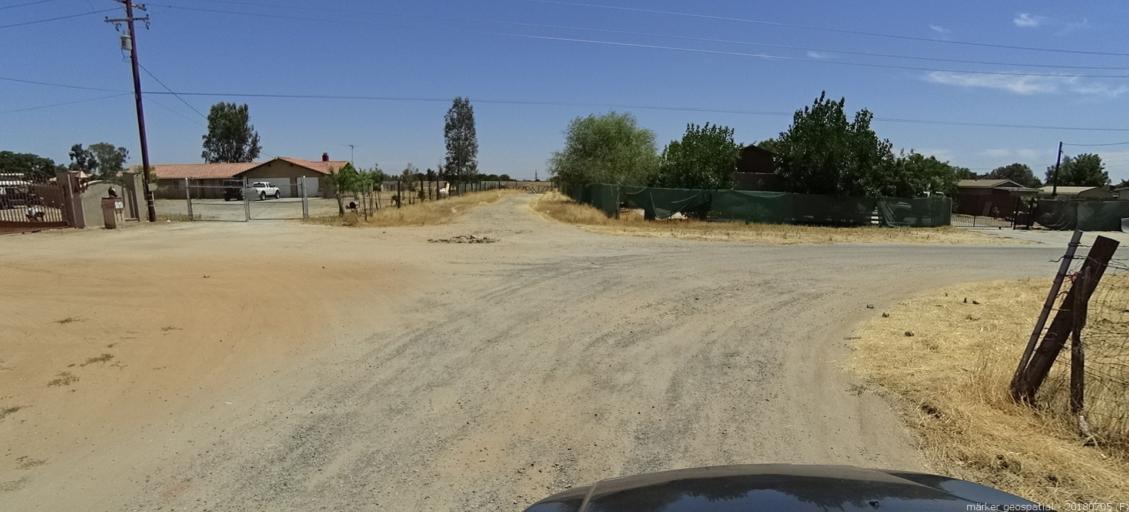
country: US
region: California
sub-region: Madera County
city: Madera
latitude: 36.9866
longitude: -120.0344
